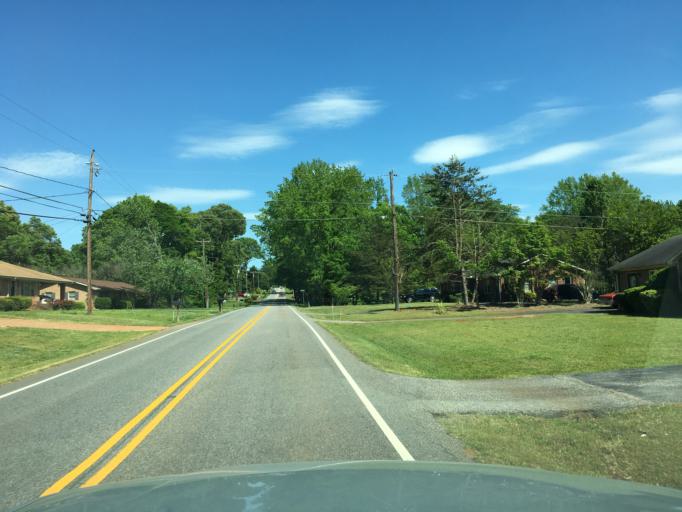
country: US
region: South Carolina
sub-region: Spartanburg County
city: Fairforest
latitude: 34.9698
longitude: -82.0384
